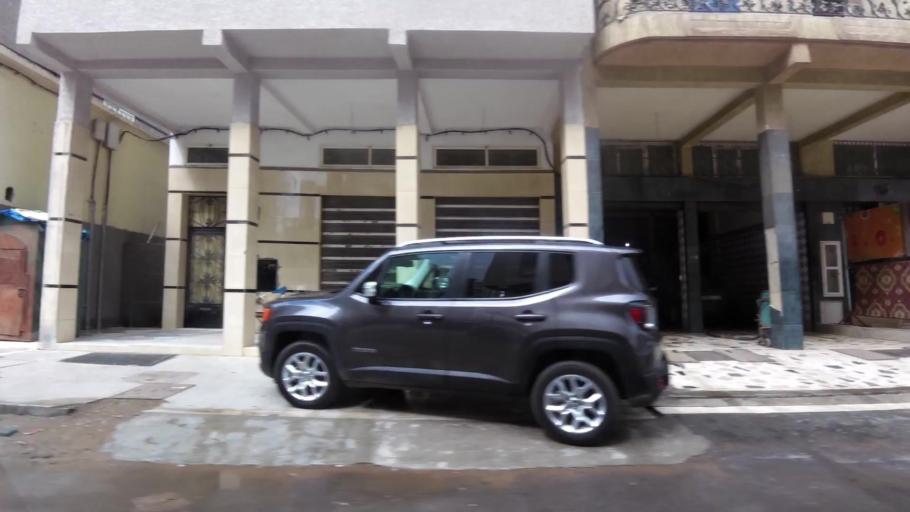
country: MA
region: Grand Casablanca
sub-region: Nouaceur
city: Bouskoura
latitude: 33.5185
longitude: -7.6516
